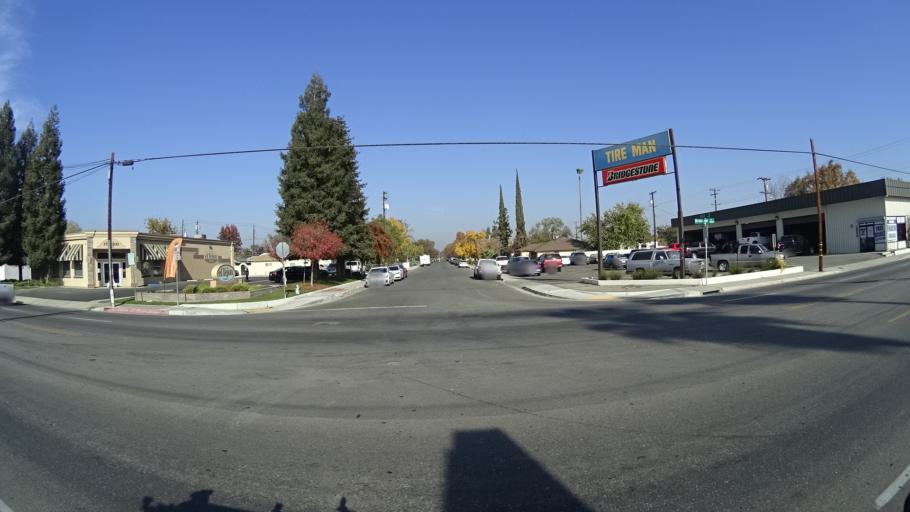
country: US
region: California
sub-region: Kern County
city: Bakersfield
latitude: 35.3541
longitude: -119.0351
